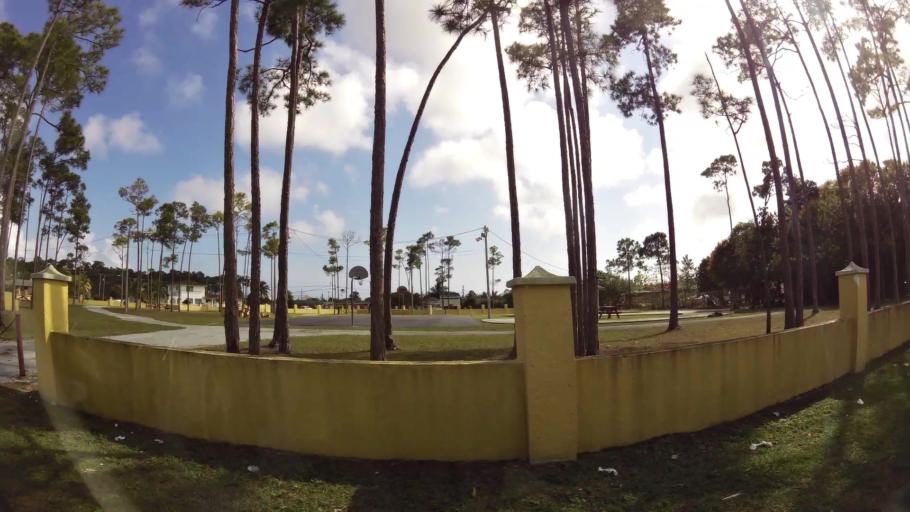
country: BS
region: Freeport
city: Lucaya
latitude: 26.5353
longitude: -78.6729
